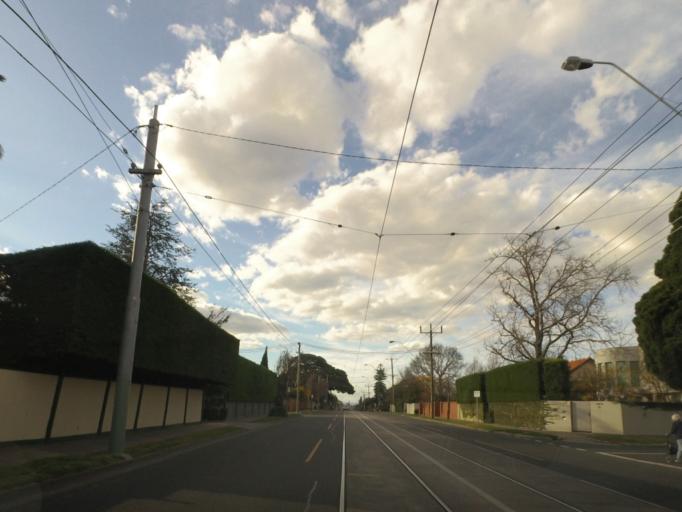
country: AU
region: Victoria
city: Glenferrie
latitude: -37.8376
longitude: 145.0554
